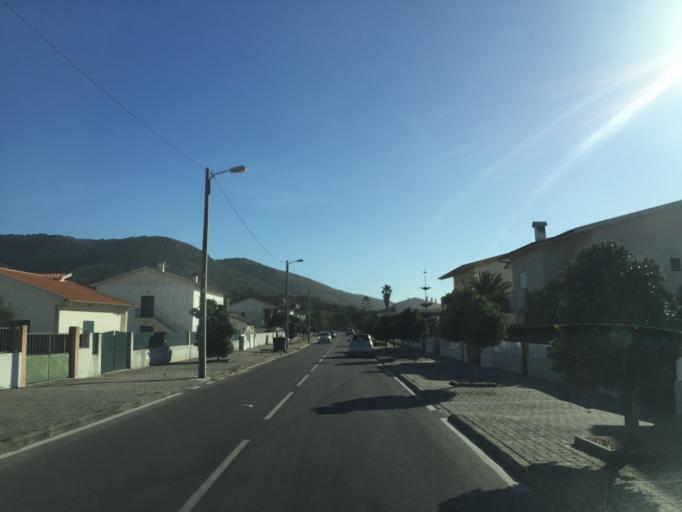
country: PT
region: Coimbra
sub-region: Figueira da Foz
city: Buarcos
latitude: 40.2147
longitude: -8.8915
